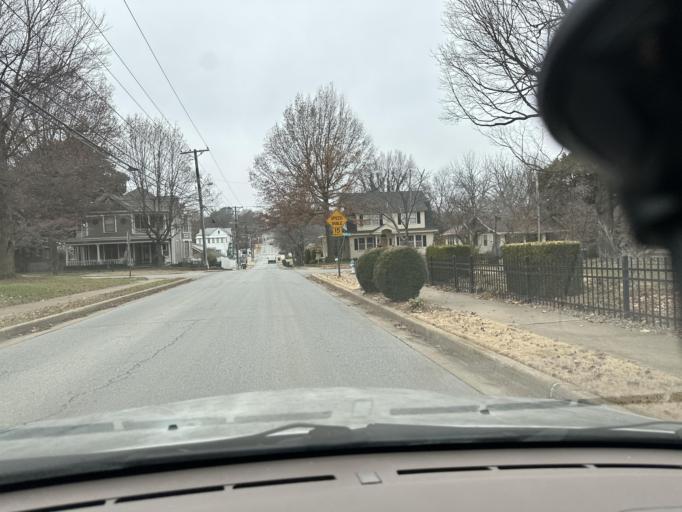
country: US
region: Arkansas
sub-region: Washington County
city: Fayetteville
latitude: 36.0699
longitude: -94.1557
